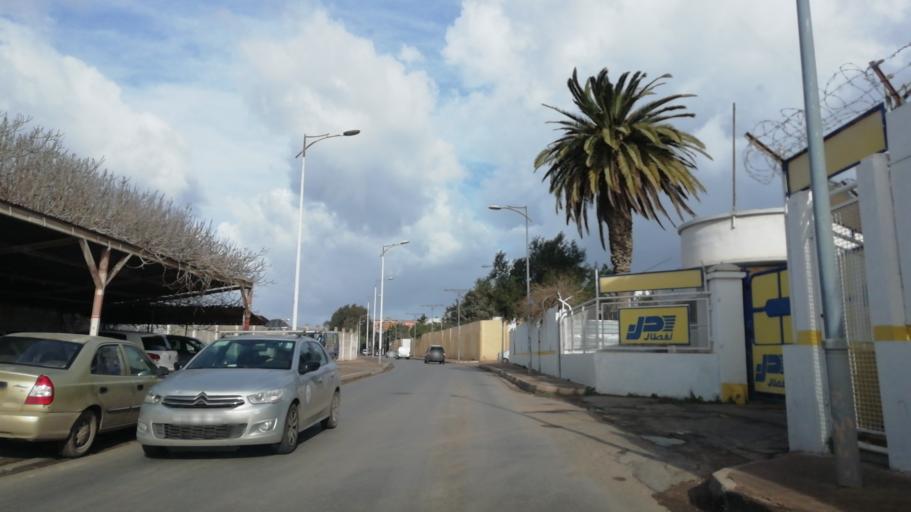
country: DZ
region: Oran
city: Oran
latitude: 35.6802
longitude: -0.6252
